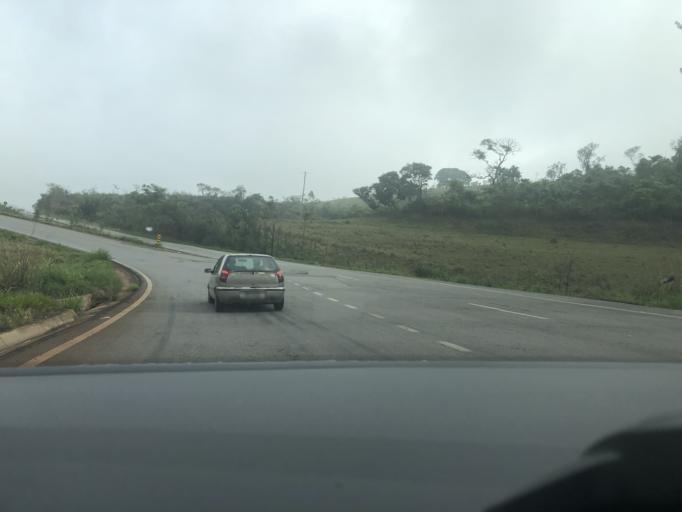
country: BR
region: Minas Gerais
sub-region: Congonhas
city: Congonhas
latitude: -20.5840
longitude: -43.9454
